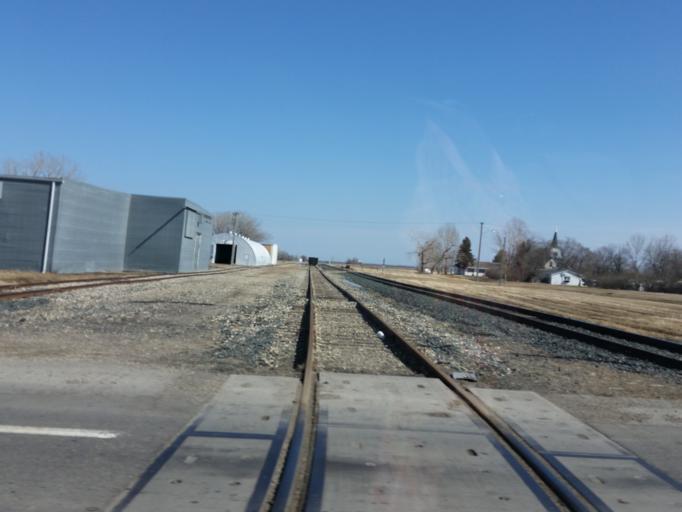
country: US
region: North Dakota
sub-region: Walsh County
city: Grafton
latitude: 48.2073
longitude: -97.3423
